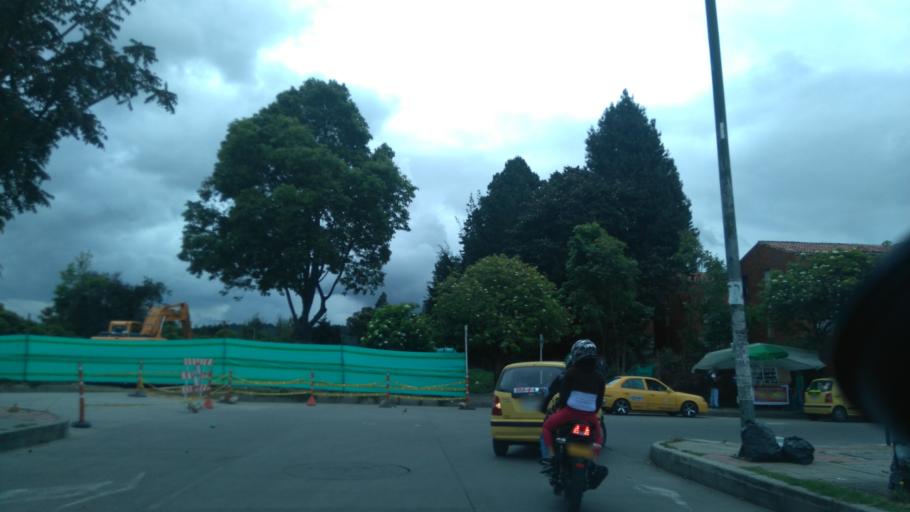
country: CO
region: Cundinamarca
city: Cota
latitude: 4.7629
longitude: -74.0495
